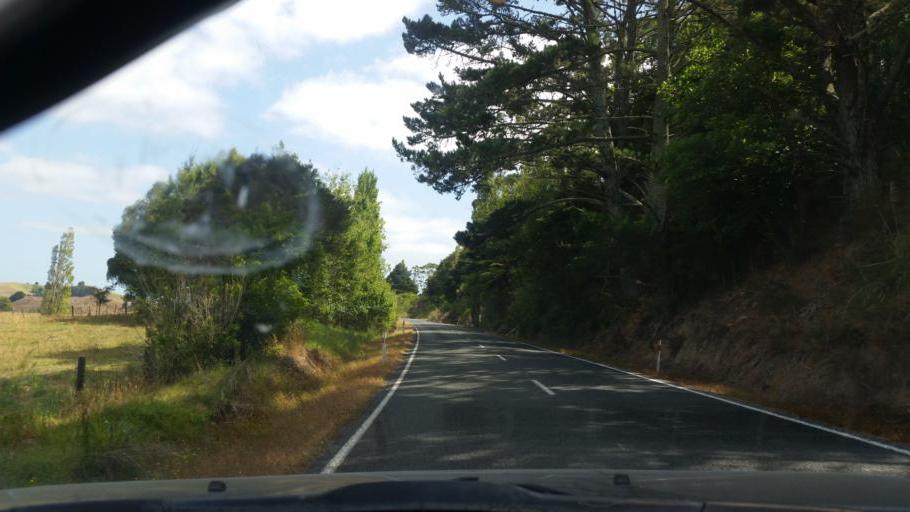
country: NZ
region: Northland
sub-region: Whangarei
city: Ruakaka
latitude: -35.9486
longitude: 174.2937
